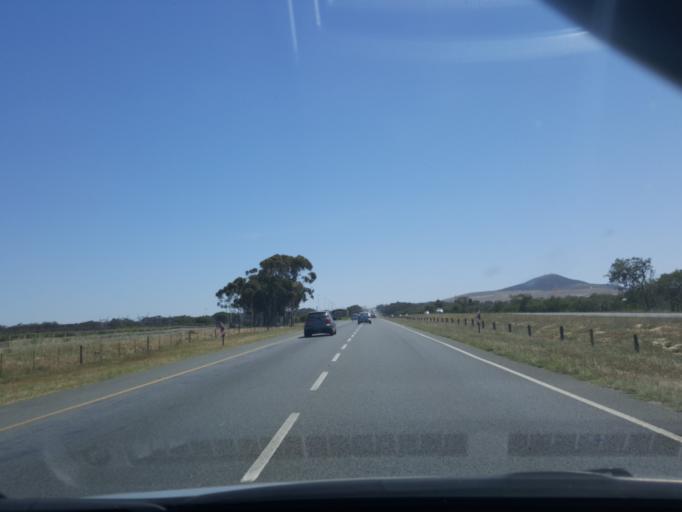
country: ZA
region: Western Cape
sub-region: City of Cape Town
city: Sunset Beach
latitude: -33.7636
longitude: 18.5474
